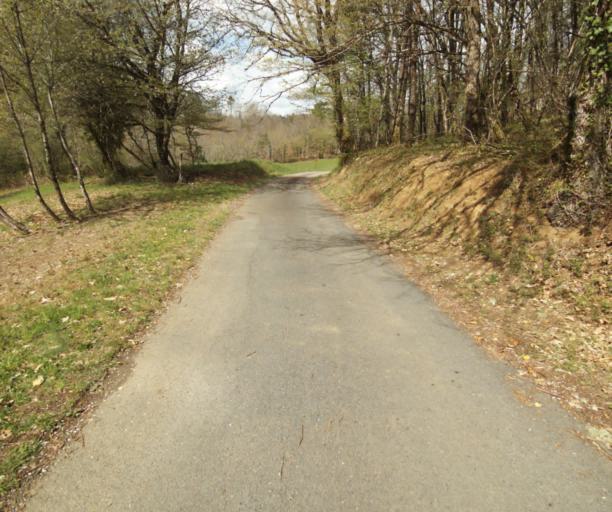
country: FR
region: Limousin
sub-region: Departement de la Correze
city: Sainte-Fortunade
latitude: 45.1854
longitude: 1.8709
